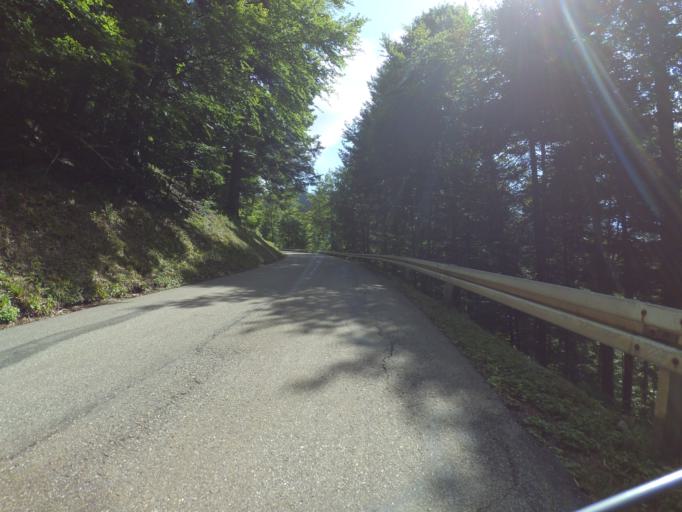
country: DE
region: Baden-Wuerttemberg
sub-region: Freiburg Region
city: Waldkirch
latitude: 48.0745
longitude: 8.0031
